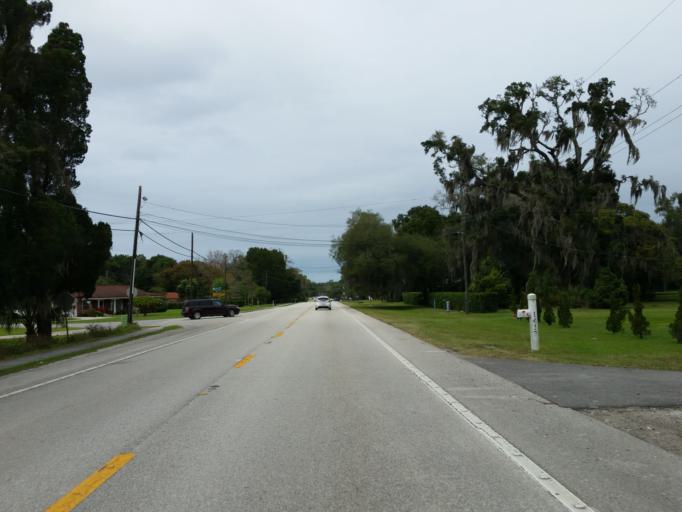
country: US
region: Florida
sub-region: Hillsborough County
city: Brandon
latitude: 27.9179
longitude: -82.2652
